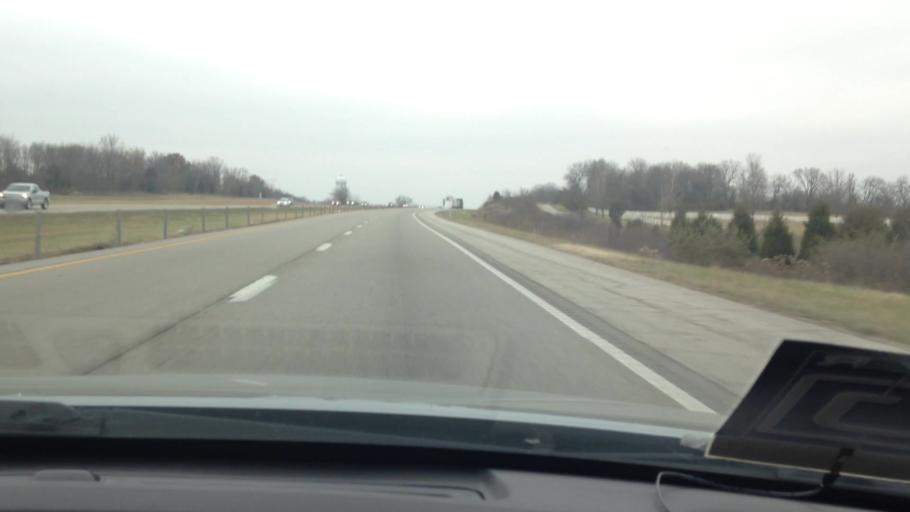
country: US
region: Missouri
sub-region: Cass County
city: Peculiar
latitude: 38.7441
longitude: -94.4746
